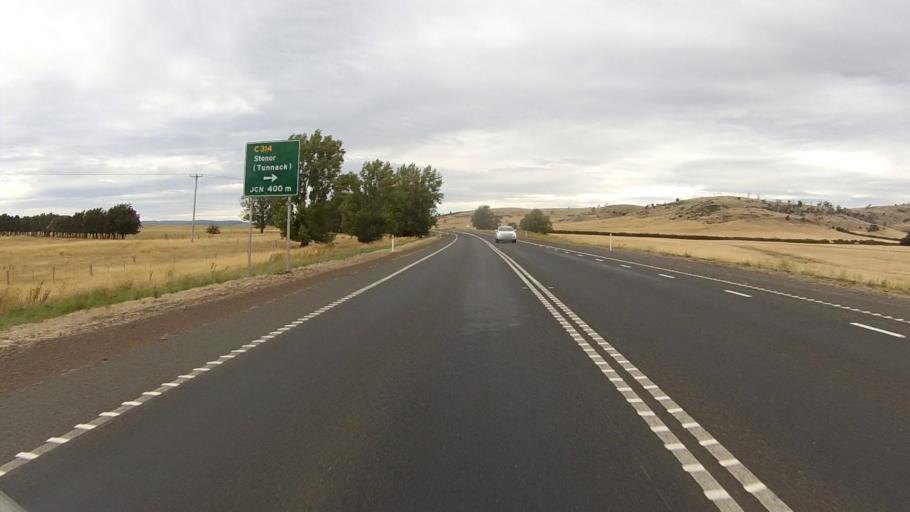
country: AU
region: Tasmania
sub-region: Brighton
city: Bridgewater
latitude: -42.3686
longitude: 147.3342
